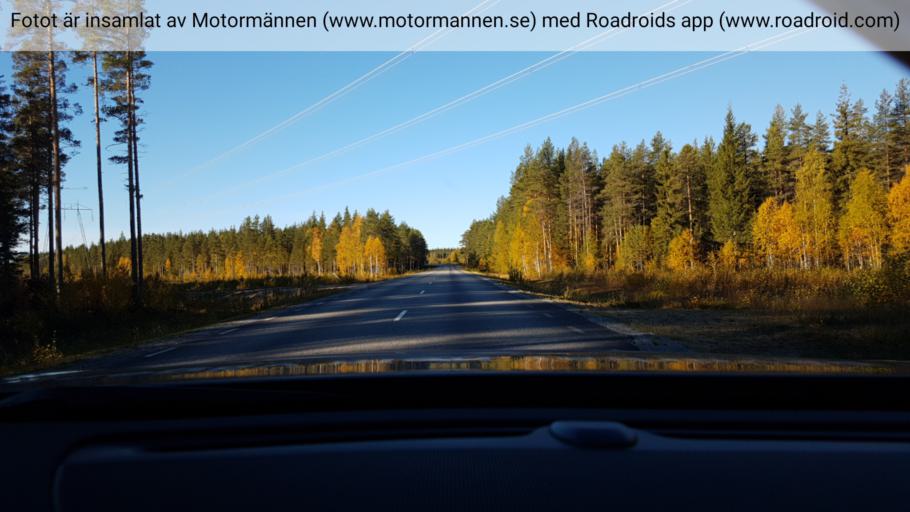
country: SE
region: Norrbotten
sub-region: Pitea Kommun
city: Roknas
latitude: 65.3521
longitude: 21.0294
